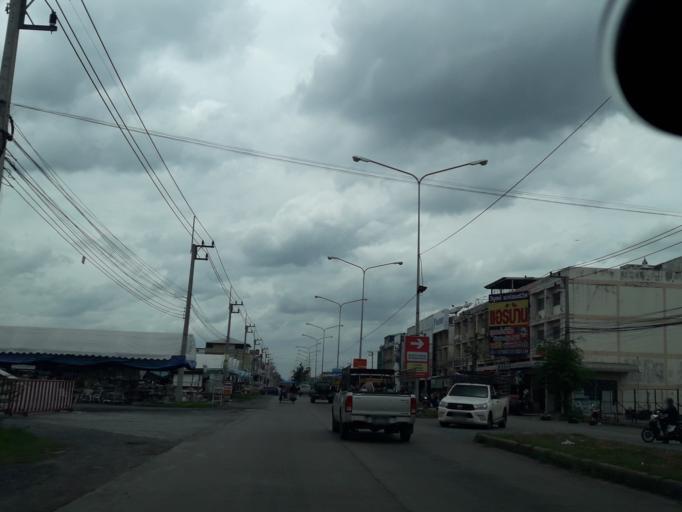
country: TH
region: Pathum Thani
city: Khlong Luang
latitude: 14.0730
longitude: 100.6339
